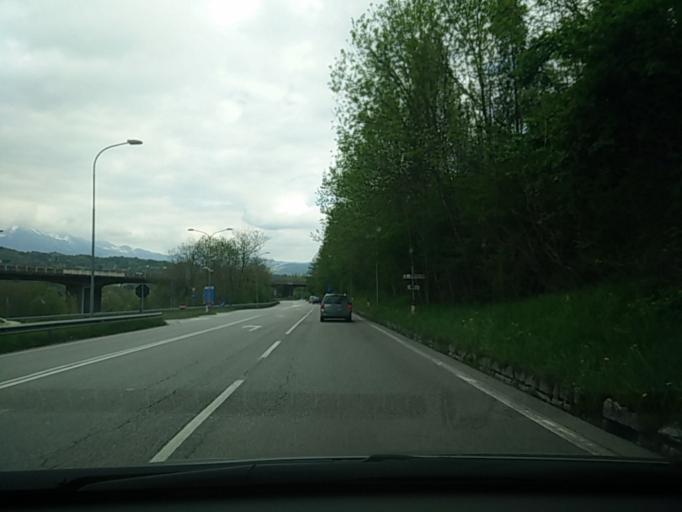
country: IT
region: Veneto
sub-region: Provincia di Belluno
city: Soccher-Paiane-Casan-Arsie
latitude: 46.1721
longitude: 12.3065
